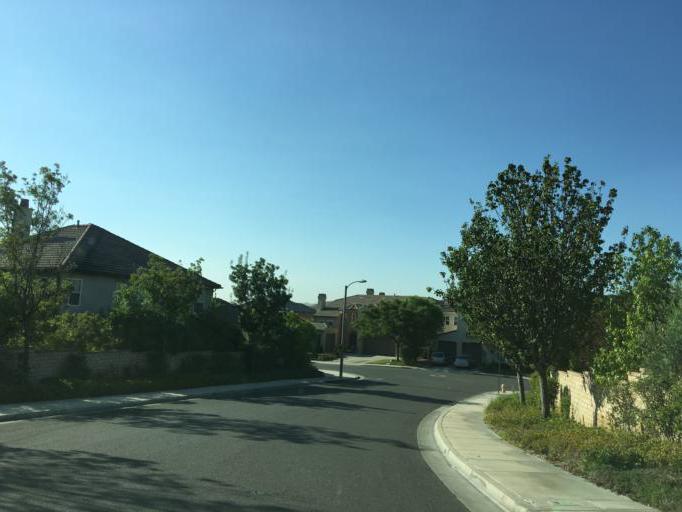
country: US
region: California
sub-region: Los Angeles County
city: Valencia
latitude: 34.4082
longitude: -118.5930
